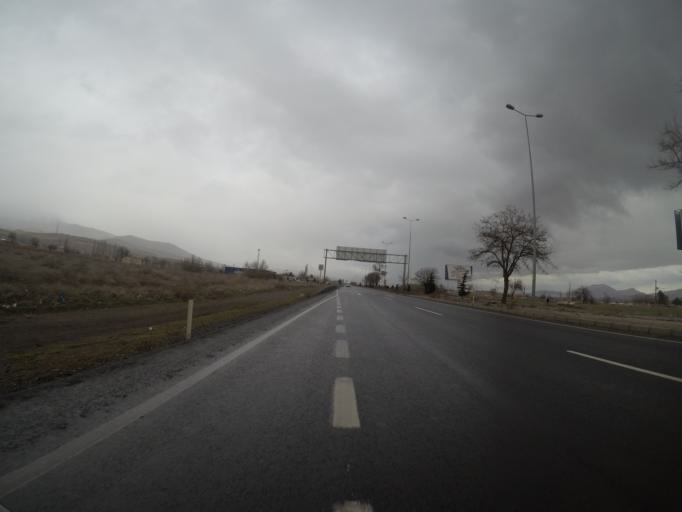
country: TR
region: Kayseri
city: Incesu
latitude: 38.6828
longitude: 35.2361
